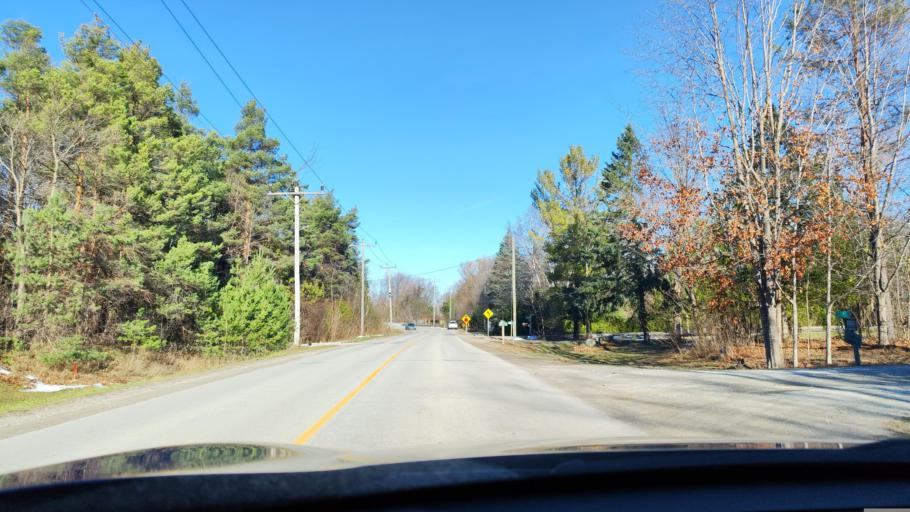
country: CA
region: Ontario
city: Collingwood
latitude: 44.4642
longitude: -80.1736
